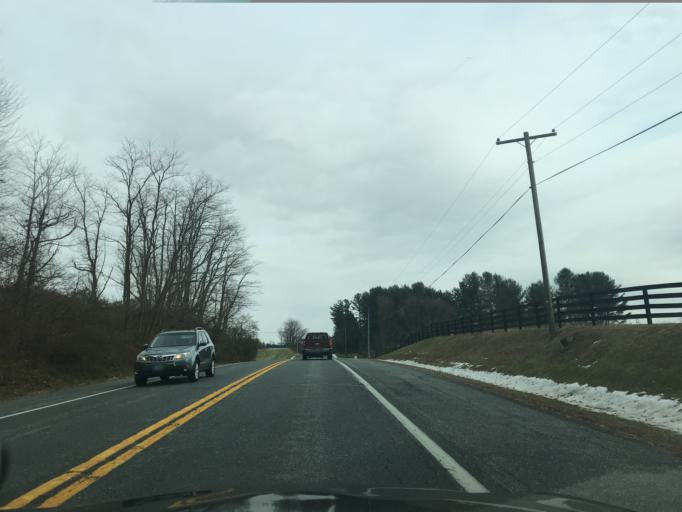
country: US
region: Maryland
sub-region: Harford County
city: Jarrettsville
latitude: 39.6657
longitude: -76.4372
